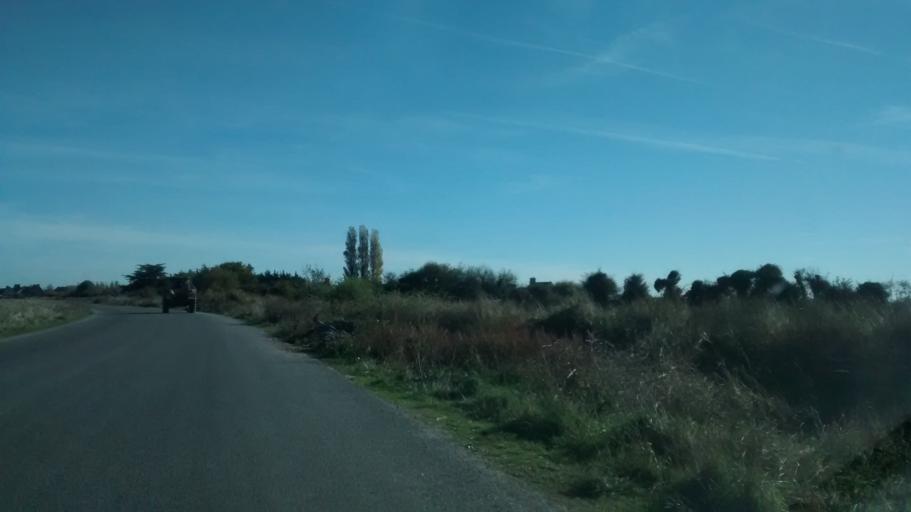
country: FR
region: Brittany
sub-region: Departement d'Ille-et-Vilaine
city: Le Vivier-sur-Mer
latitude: 48.6036
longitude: -1.7614
